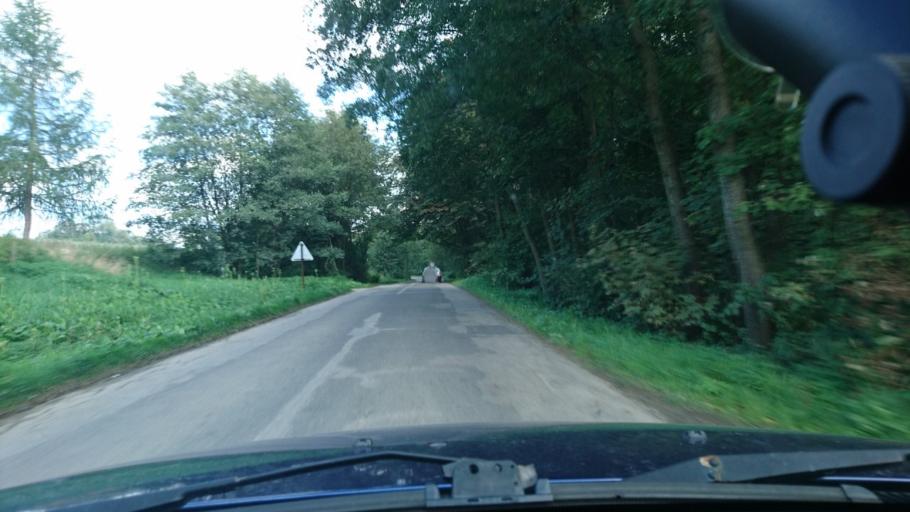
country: PL
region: Silesian Voivodeship
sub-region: Powiat bielski
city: Mazancowice
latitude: 49.8524
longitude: 18.9476
